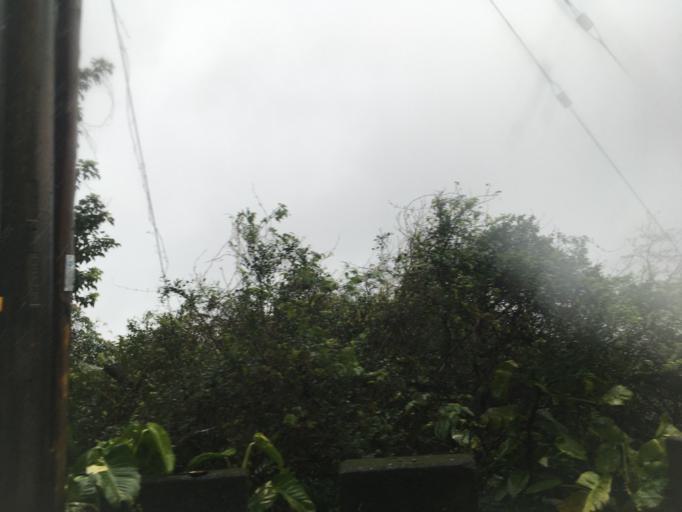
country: TW
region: Taiwan
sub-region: Keelung
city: Keelung
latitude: 25.0661
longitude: 121.9020
